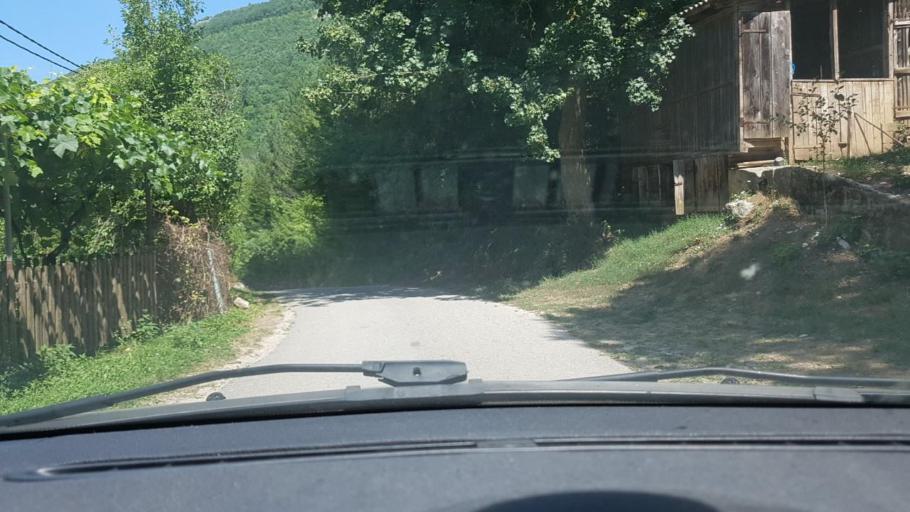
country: BA
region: Federation of Bosnia and Herzegovina
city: Orasac
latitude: 44.4912
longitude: 16.1440
